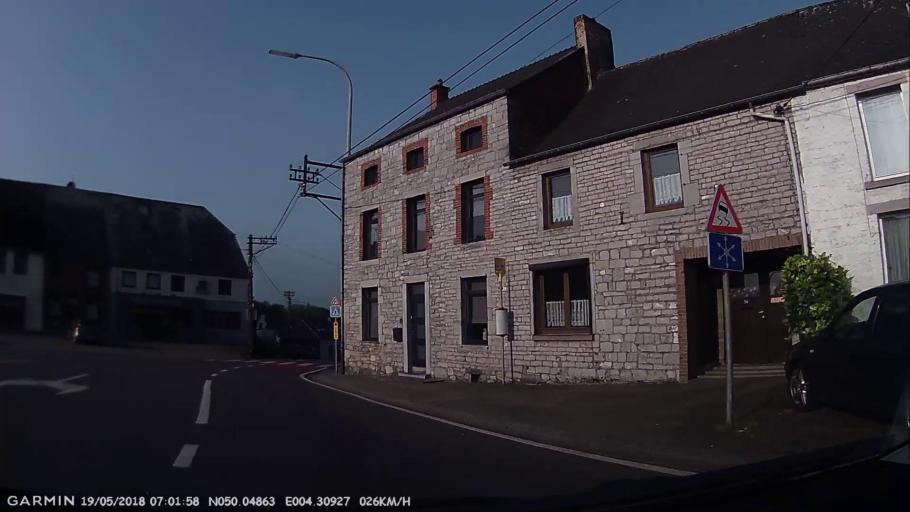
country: BE
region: Wallonia
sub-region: Province du Hainaut
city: Chimay
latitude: 50.0481
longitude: 4.3084
